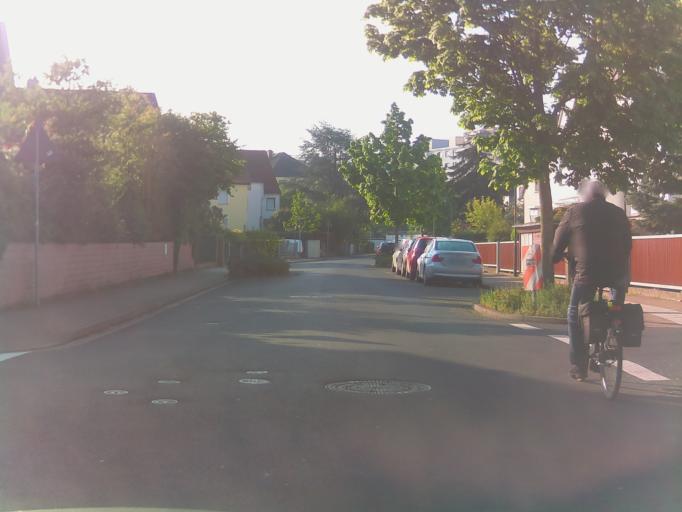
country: DE
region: Hesse
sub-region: Regierungsbezirk Darmstadt
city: Maintal
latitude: 50.1501
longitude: 8.8061
